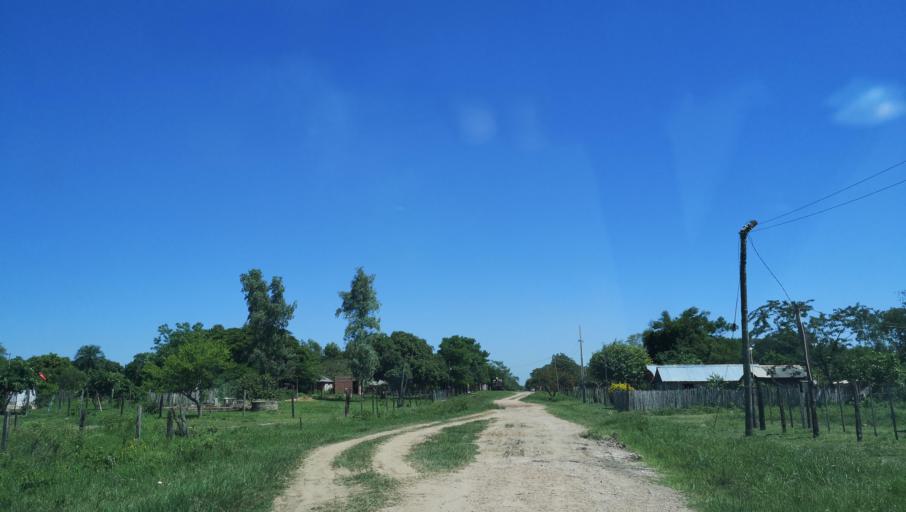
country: PY
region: Caaguazu
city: Carayao
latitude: -25.1935
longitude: -56.3963
